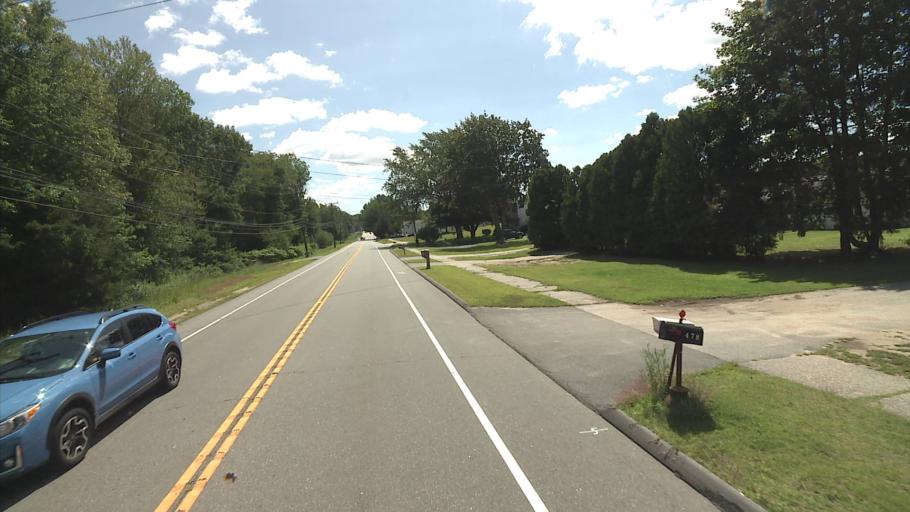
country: US
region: Connecticut
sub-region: New London County
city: Niantic
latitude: 41.3616
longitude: -72.1785
